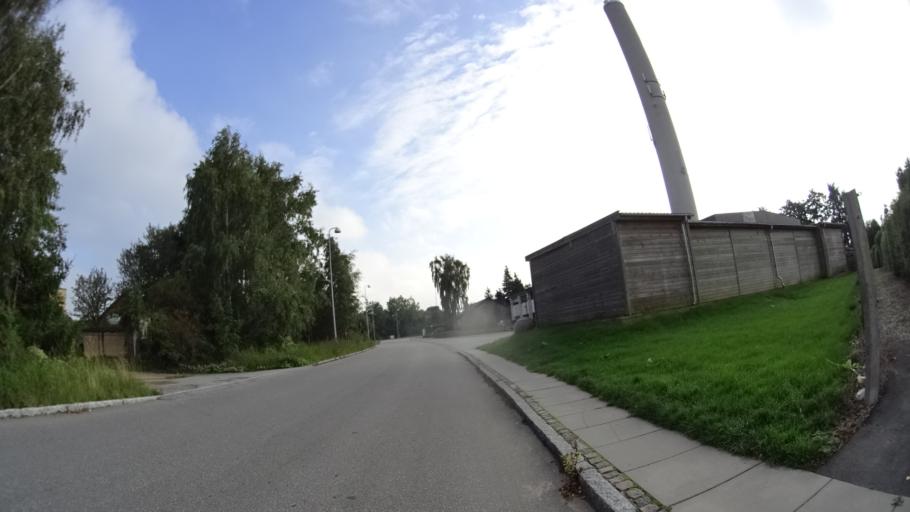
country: DK
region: Central Jutland
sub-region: Arhus Kommune
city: Arhus
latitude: 56.1367
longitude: 10.1727
